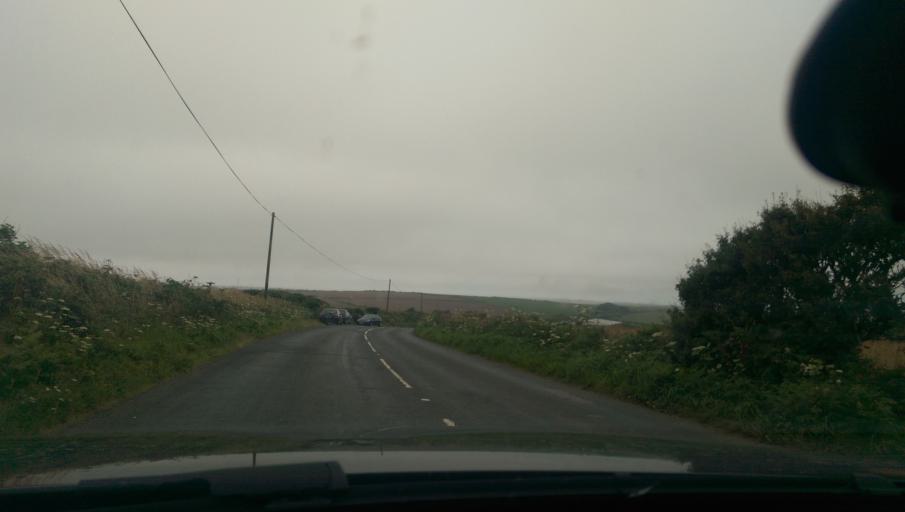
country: GB
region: England
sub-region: Cornwall
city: St. Buryan
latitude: 50.0933
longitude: -5.6219
